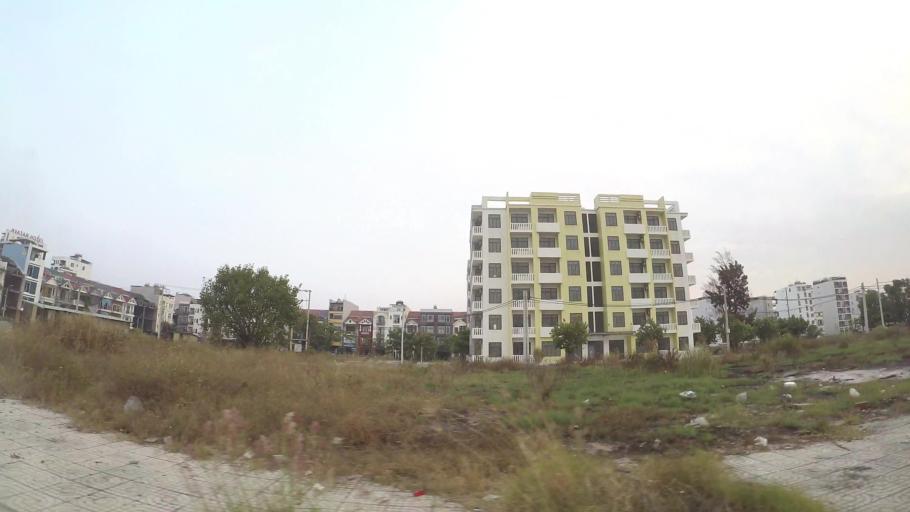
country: VN
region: Da Nang
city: Son Tra
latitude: 16.0505
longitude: 108.2434
